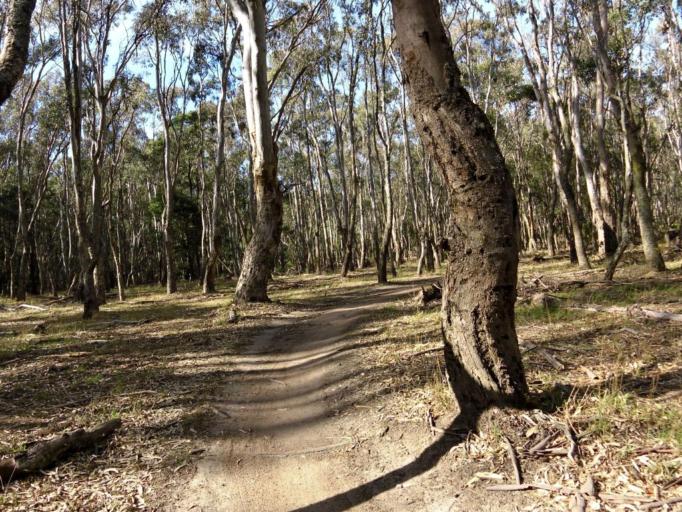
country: AU
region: Victoria
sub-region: Yarra Ranges
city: Lysterfield
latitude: -37.9365
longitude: 145.2955
